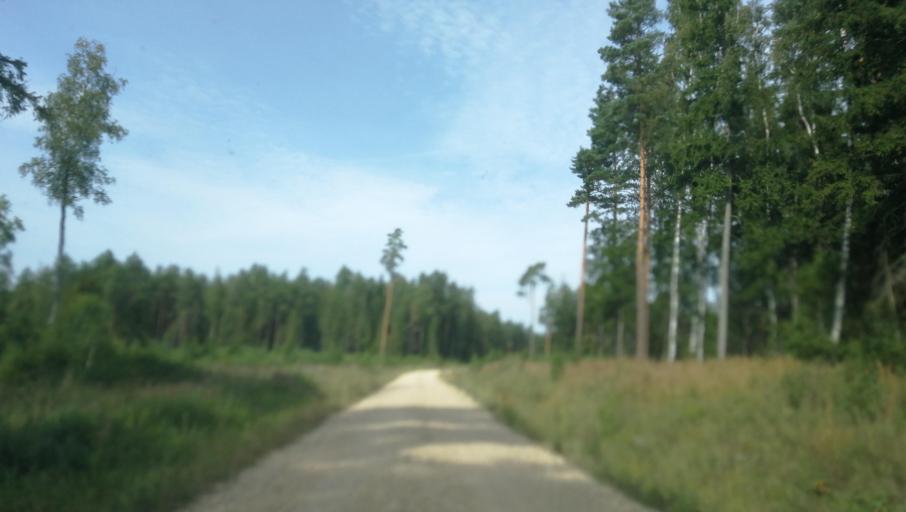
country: LV
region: Pavilostas
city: Pavilosta
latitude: 56.8148
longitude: 21.3346
